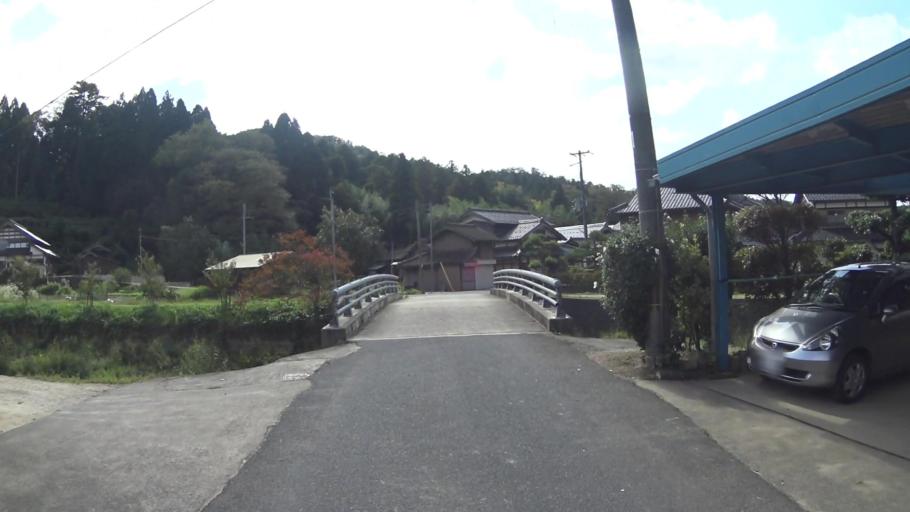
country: JP
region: Kyoto
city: Miyazu
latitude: 35.6565
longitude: 135.1131
